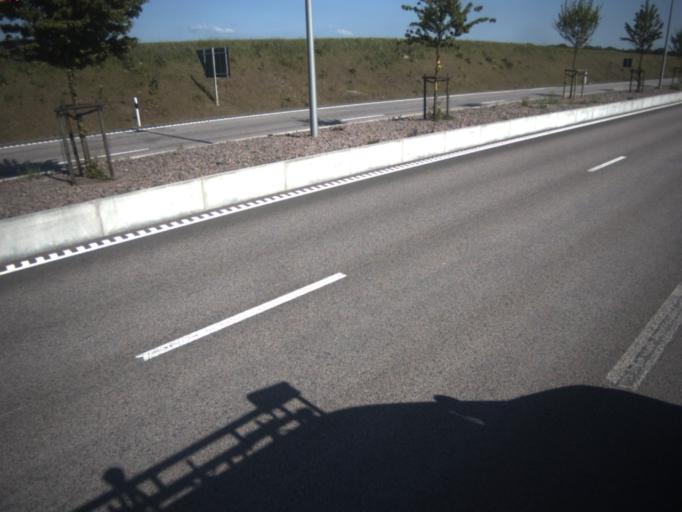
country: SE
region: Skane
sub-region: Helsingborg
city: Helsingborg
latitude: 56.0367
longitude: 12.7596
